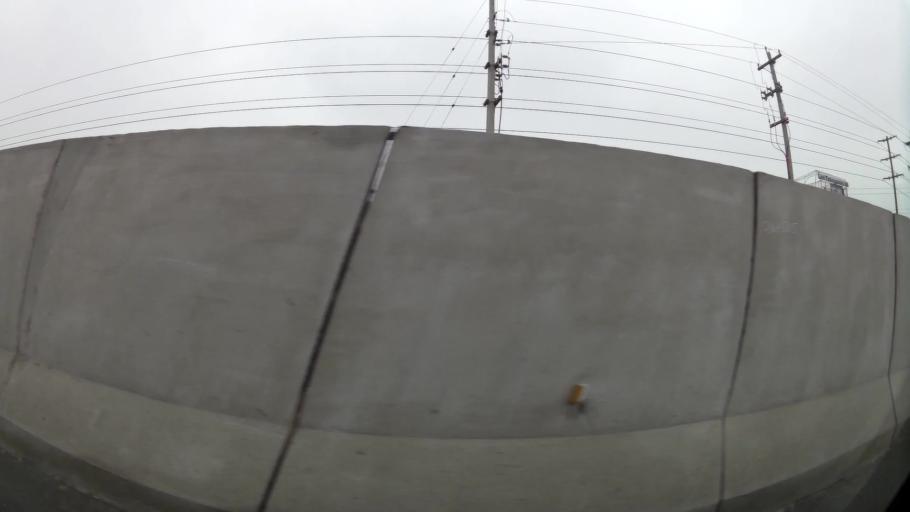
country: PE
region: Lima
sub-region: Lima
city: Urb. Santo Domingo
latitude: -11.9005
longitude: -77.0677
